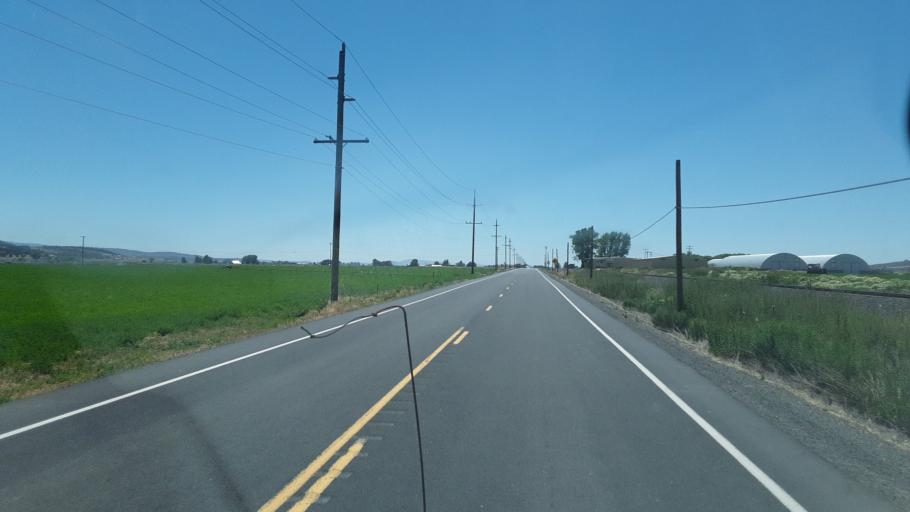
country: US
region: Oregon
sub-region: Klamath County
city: Altamont
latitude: 42.0682
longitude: -121.6627
